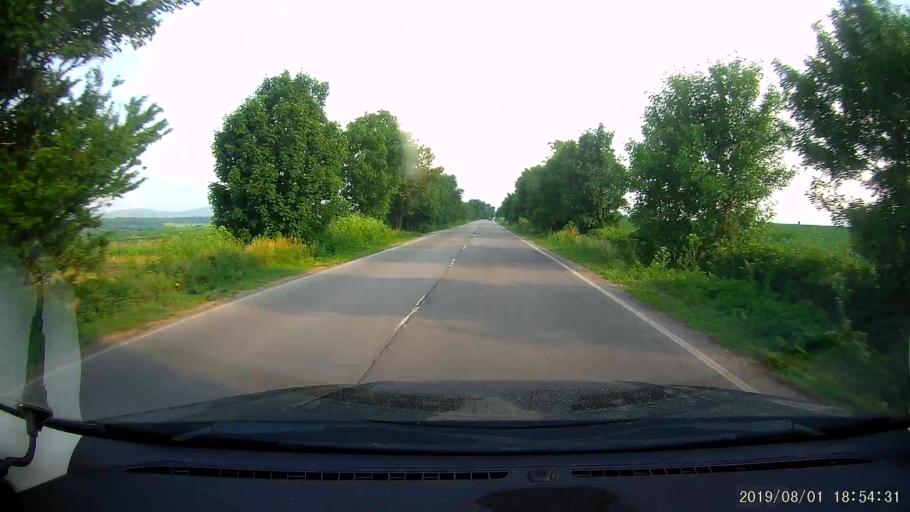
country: BG
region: Shumen
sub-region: Obshtina Shumen
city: Shumen
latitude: 43.1964
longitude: 27.0021
